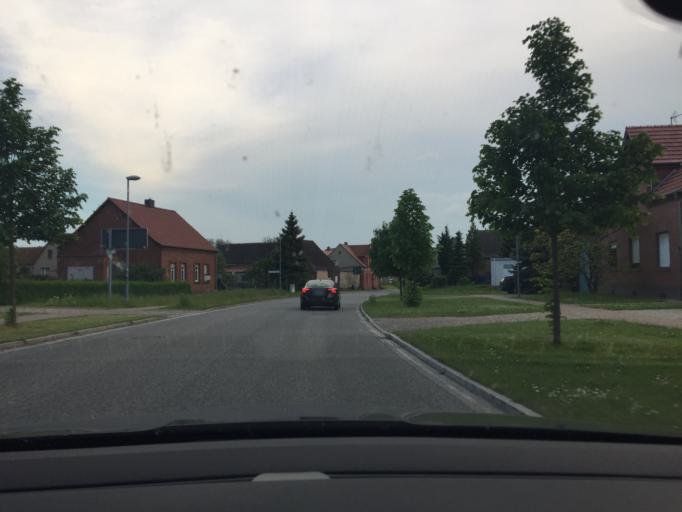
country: DE
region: Saxony-Anhalt
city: Kropstadt
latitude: 52.0037
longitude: 12.7812
